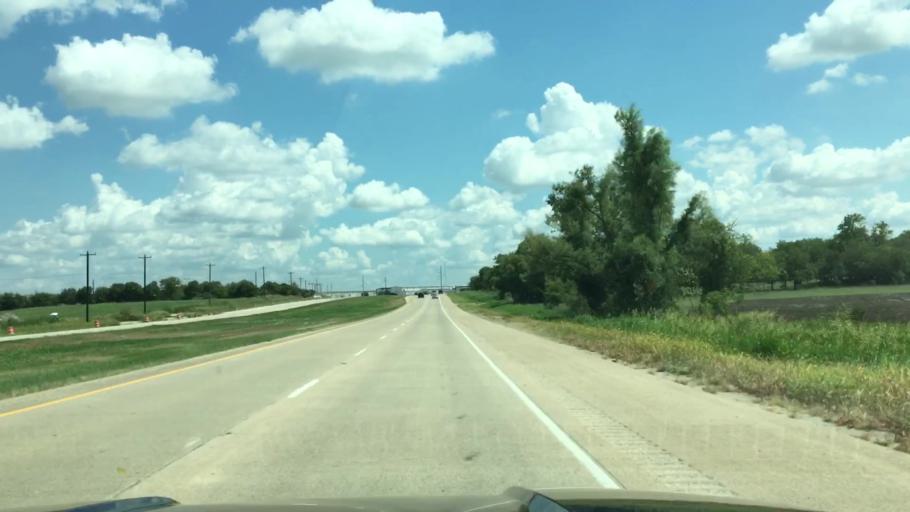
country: US
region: Texas
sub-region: Wise County
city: Rhome
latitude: 33.0403
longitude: -97.4466
